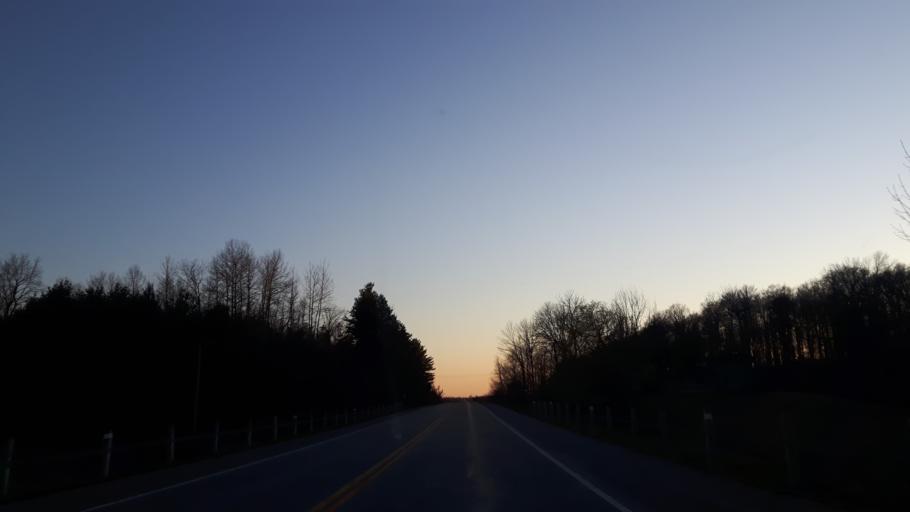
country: CA
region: Ontario
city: Bluewater
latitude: 43.5934
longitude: -81.5690
